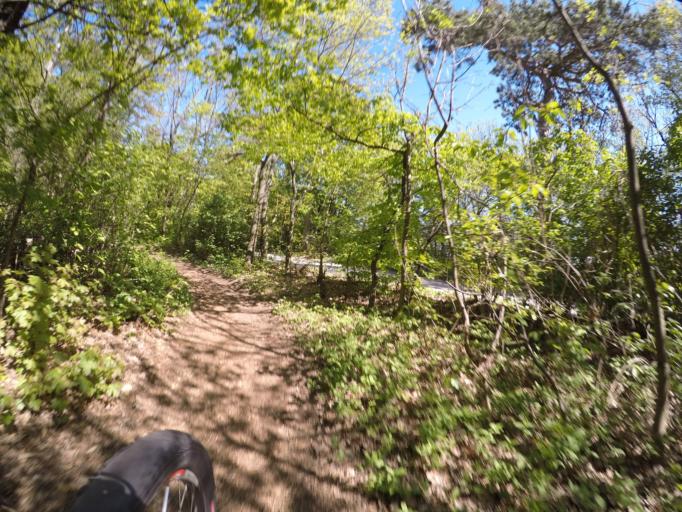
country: AT
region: Lower Austria
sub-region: Politischer Bezirk Modling
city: Gumpoldskirchen
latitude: 48.0613
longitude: 16.2788
